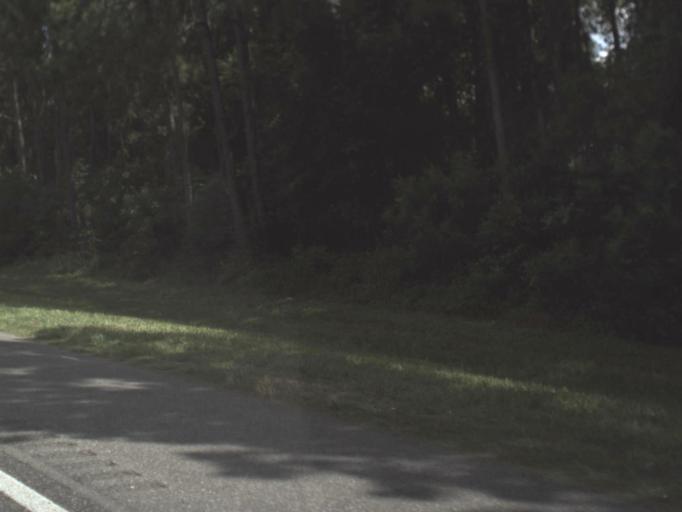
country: US
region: Florida
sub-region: Columbia County
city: Lake City
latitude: 30.0941
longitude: -82.6421
